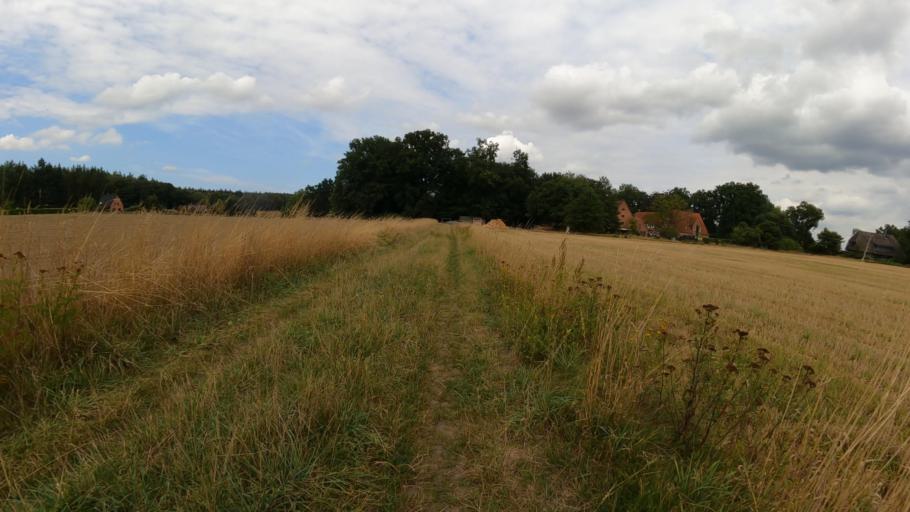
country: DE
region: Lower Saxony
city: Buchholz in der Nordheide
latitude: 53.3480
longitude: 9.9071
